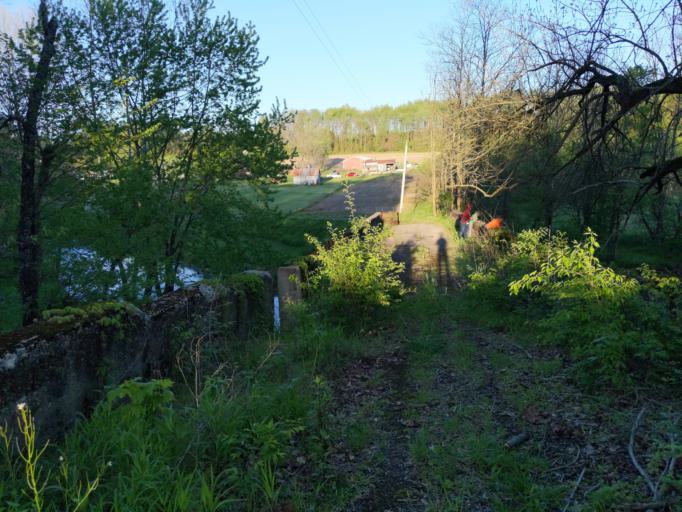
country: US
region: Indiana
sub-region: Decatur County
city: Westport
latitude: 39.1901
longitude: -85.4359
